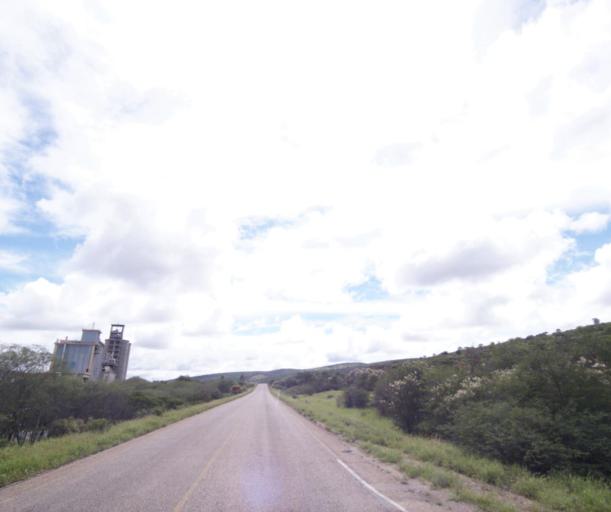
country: BR
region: Bahia
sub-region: Brumado
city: Brumado
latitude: -14.1994
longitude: -41.5998
